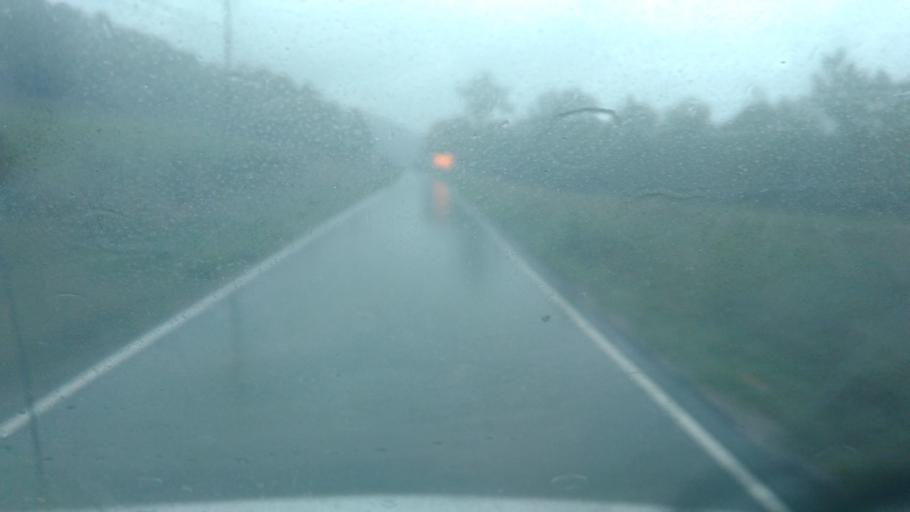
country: US
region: Kentucky
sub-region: Lewis County
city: Vanceburg
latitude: 38.5668
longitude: -83.4333
